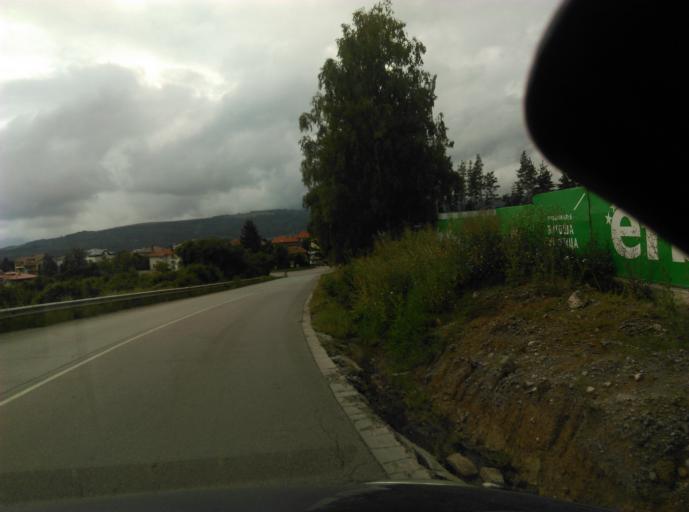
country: BG
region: Sofia-Capital
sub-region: Stolichna Obshtina
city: Sofia
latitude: 42.5919
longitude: 23.3636
